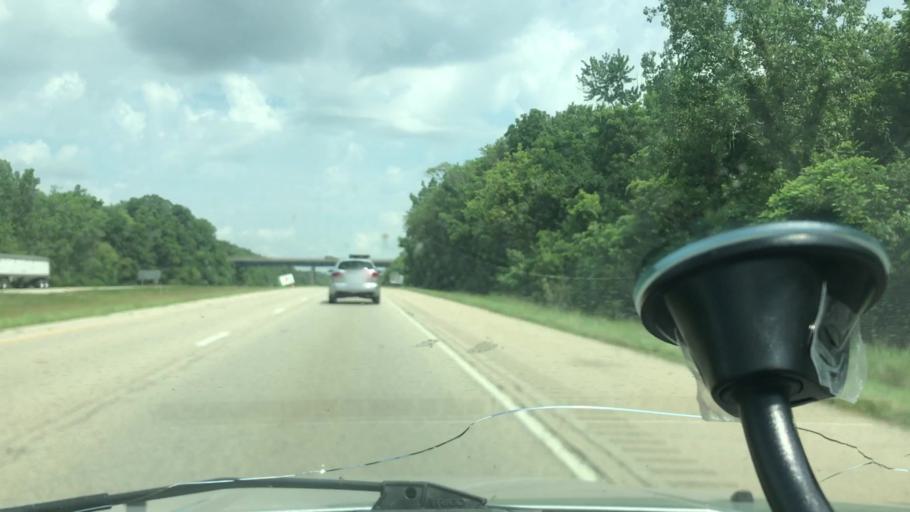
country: US
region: Illinois
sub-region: Peoria County
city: Bellevue
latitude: 40.6818
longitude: -89.6752
